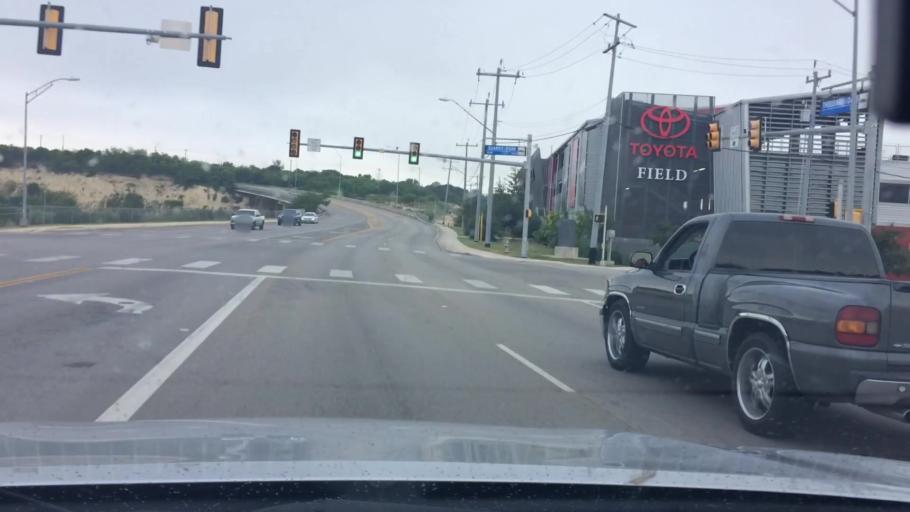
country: US
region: Texas
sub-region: Bexar County
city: Windcrest
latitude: 29.5376
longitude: -98.3959
